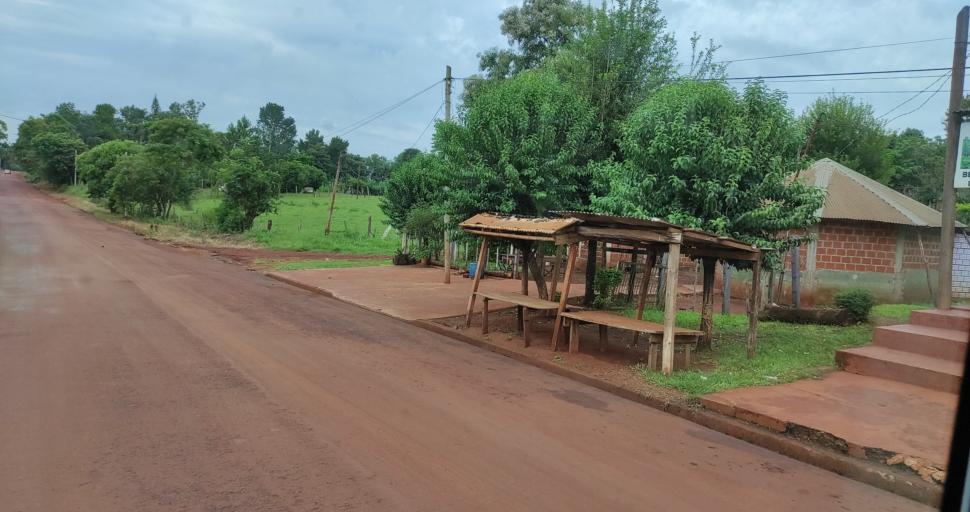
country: AR
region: Misiones
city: Puerto Libertad
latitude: -25.9620
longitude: -54.5946
